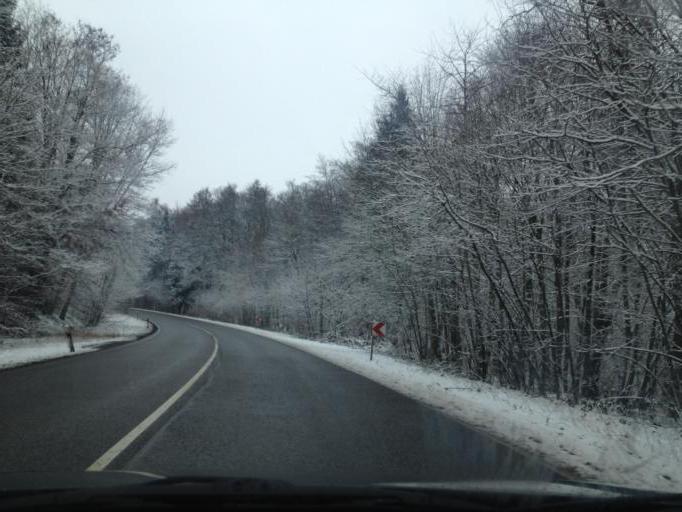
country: DE
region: Saarland
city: Schiffweiler
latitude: 49.3646
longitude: 7.1513
